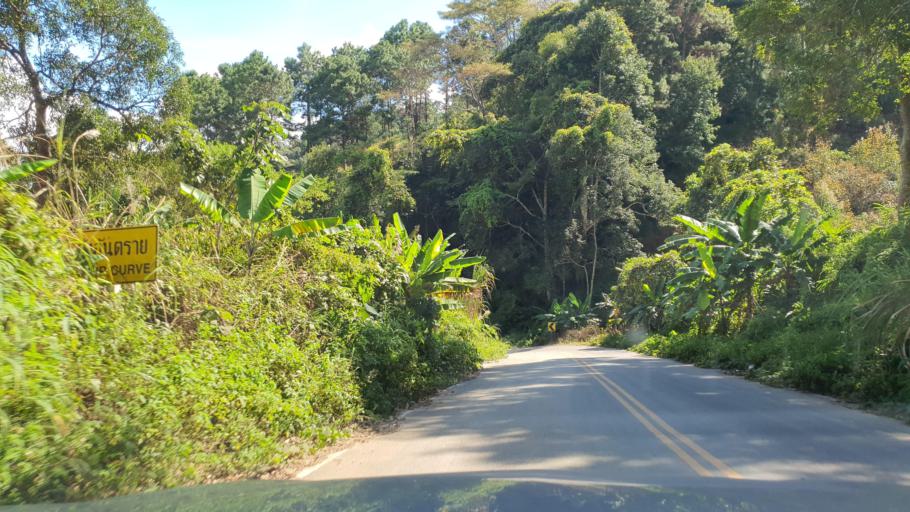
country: TH
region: Chiang Mai
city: Phrao
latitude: 19.3096
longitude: 99.3383
